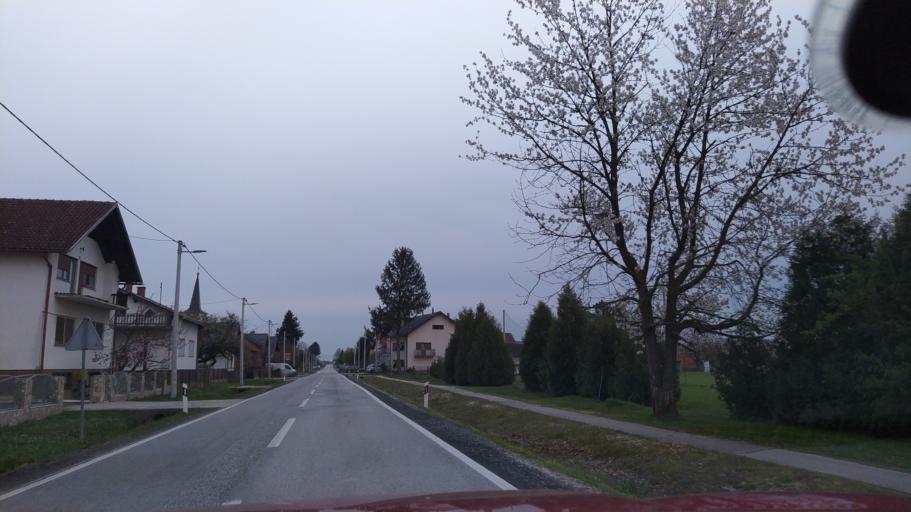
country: HR
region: Varazdinska
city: Ludbreg
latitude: 46.2502
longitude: 16.5852
